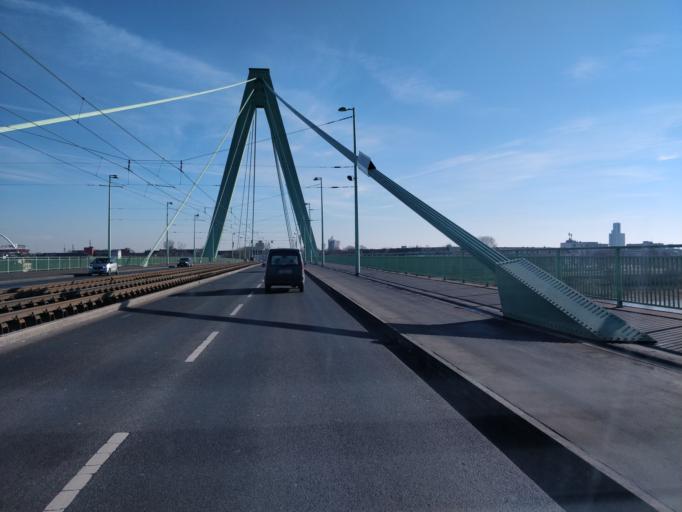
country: DE
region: North Rhine-Westphalia
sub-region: Regierungsbezirk Koln
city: Altstadt Sud
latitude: 50.9300
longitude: 6.9671
